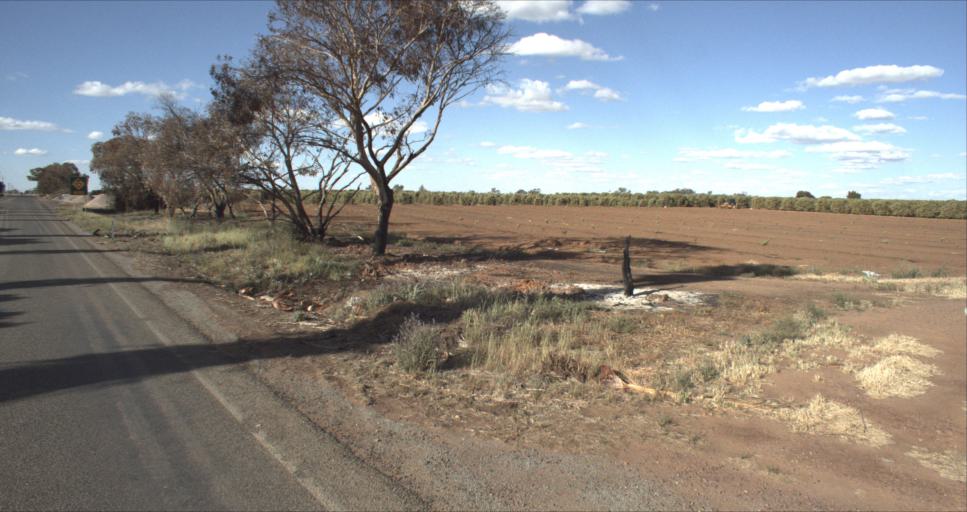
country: AU
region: New South Wales
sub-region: Leeton
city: Leeton
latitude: -34.5232
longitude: 146.2829
